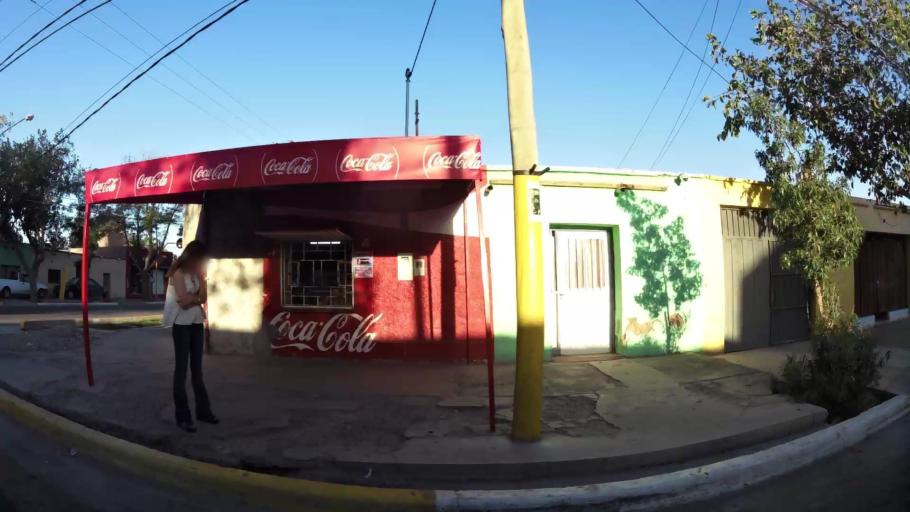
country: AR
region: San Juan
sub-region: Departamento de Santa Lucia
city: Santa Lucia
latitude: -31.5407
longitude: -68.4940
